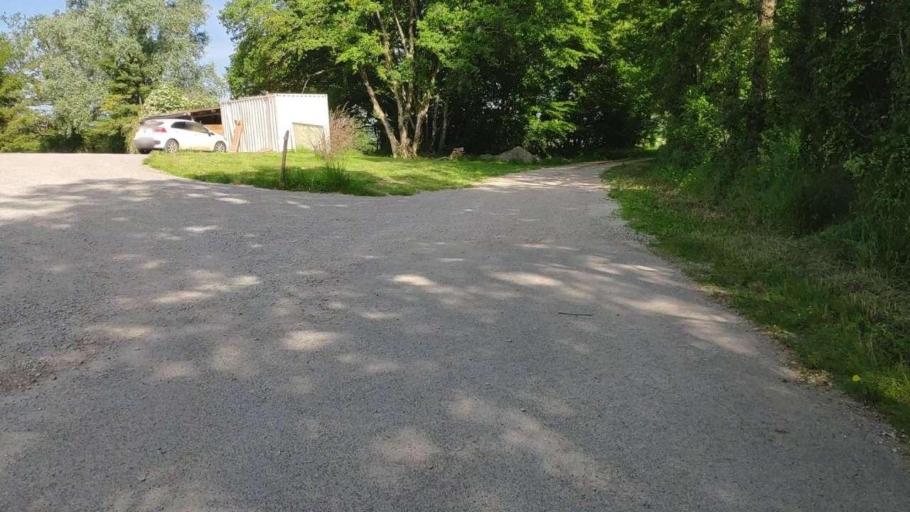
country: FR
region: Franche-Comte
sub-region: Departement du Jura
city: Bletterans
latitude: 46.7147
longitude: 5.4516
